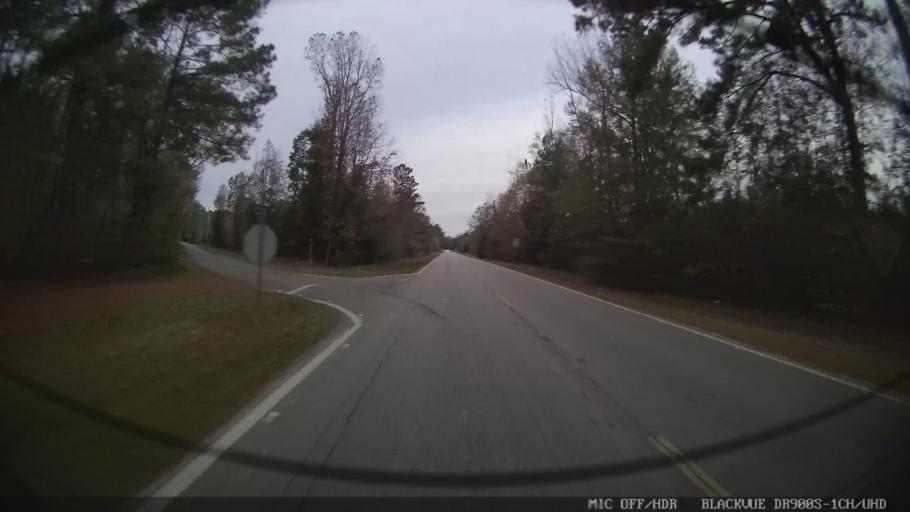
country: US
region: Mississippi
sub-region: Clarke County
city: Stonewall
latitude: 32.0358
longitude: -88.8751
